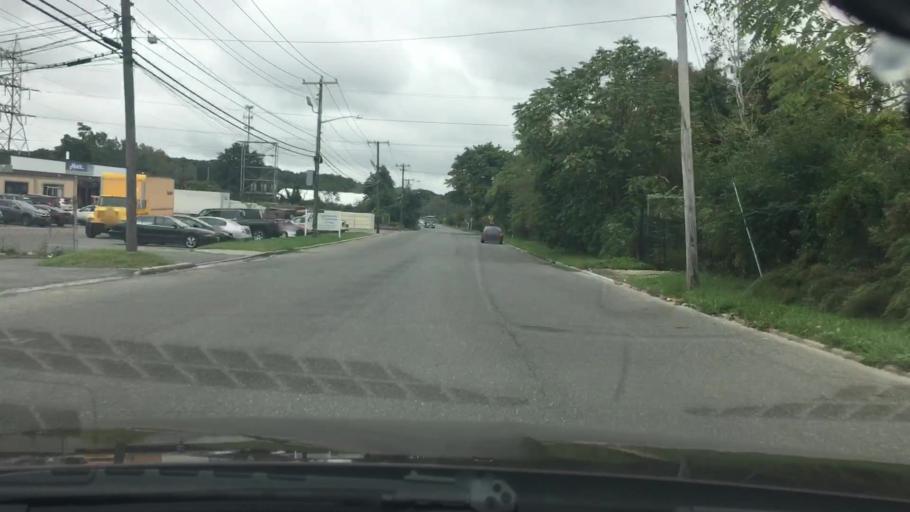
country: US
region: New York
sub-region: Nassau County
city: Old Bethpage
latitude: 40.7610
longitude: -73.4451
